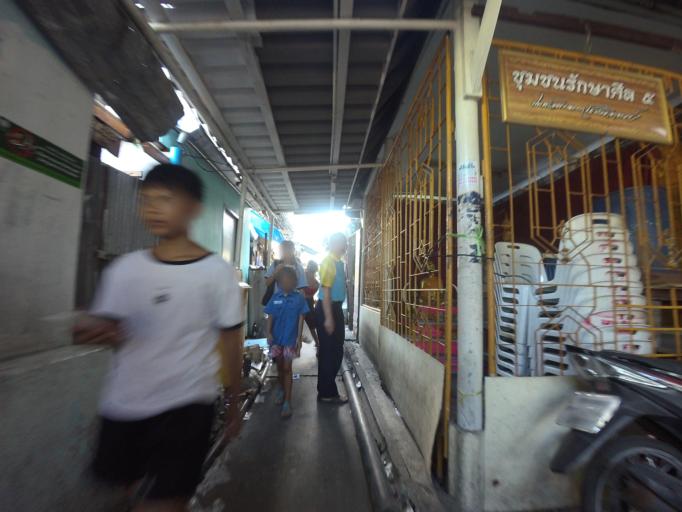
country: TH
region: Bangkok
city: Khlong Toei
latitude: 13.7120
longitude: 100.5724
